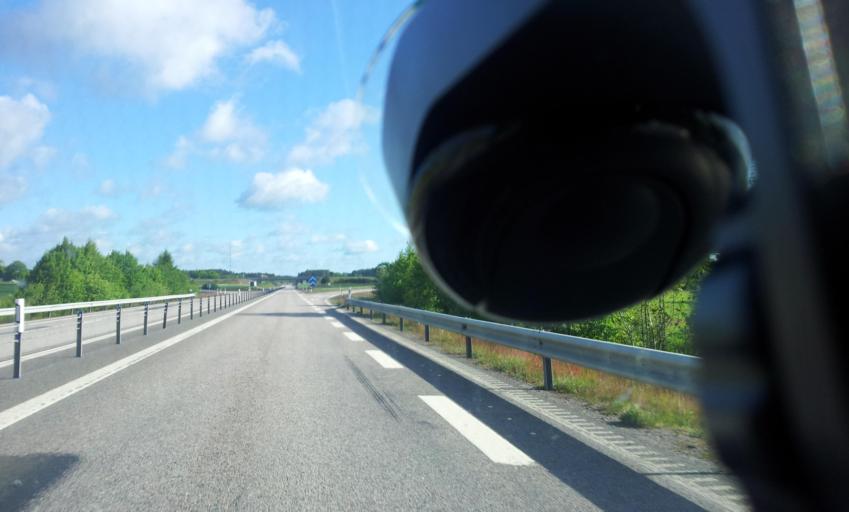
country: SE
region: Kalmar
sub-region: Torsas Kommun
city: Torsas
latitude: 56.4472
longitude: 16.0791
